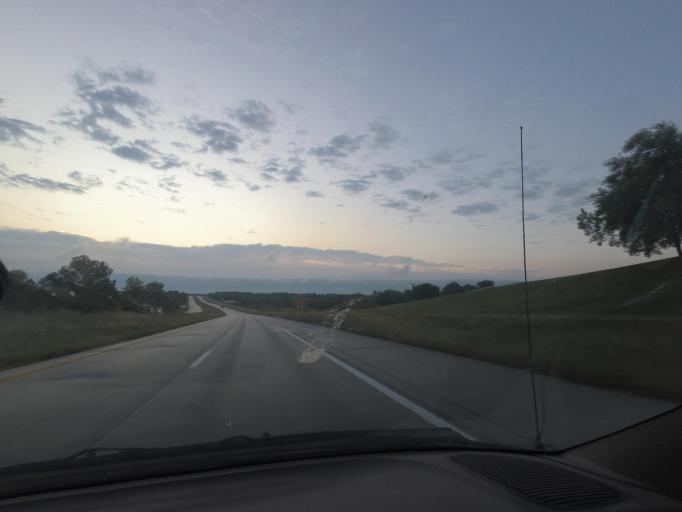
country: US
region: Missouri
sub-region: Macon County
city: Macon
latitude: 39.7494
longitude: -92.5240
